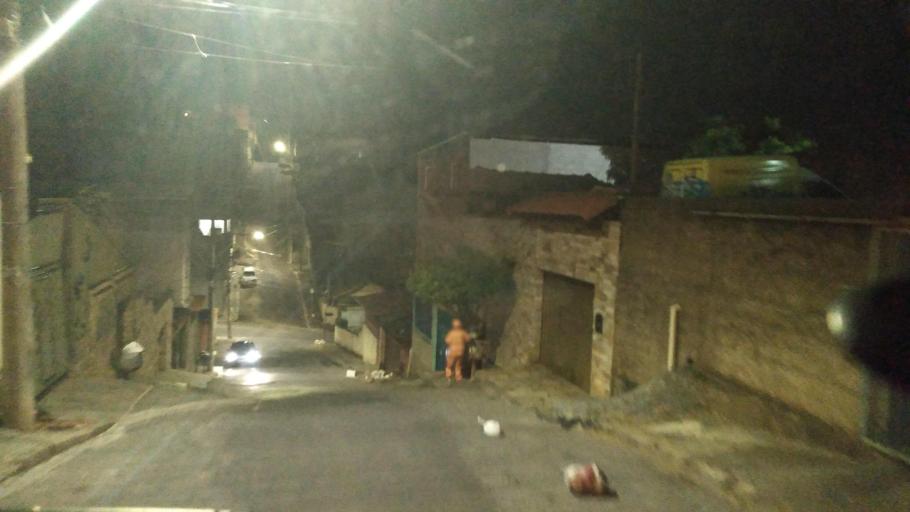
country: BR
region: Minas Gerais
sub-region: Belo Horizonte
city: Belo Horizonte
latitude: -19.8910
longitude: -43.9604
